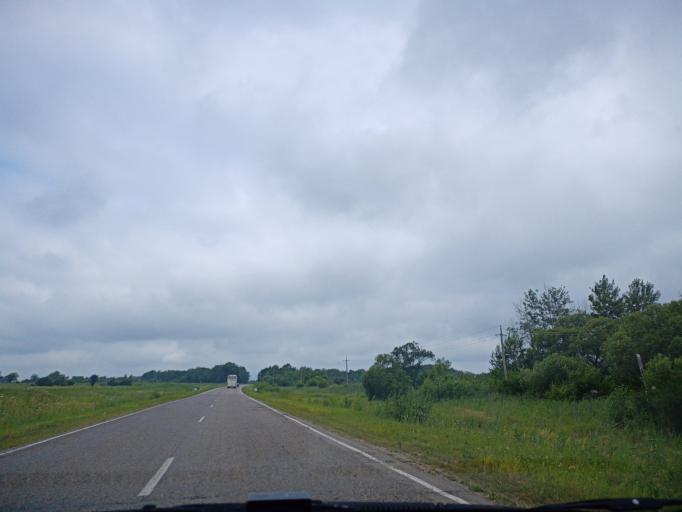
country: RU
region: Primorskiy
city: Novopokrovka
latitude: 45.9719
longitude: 134.2242
